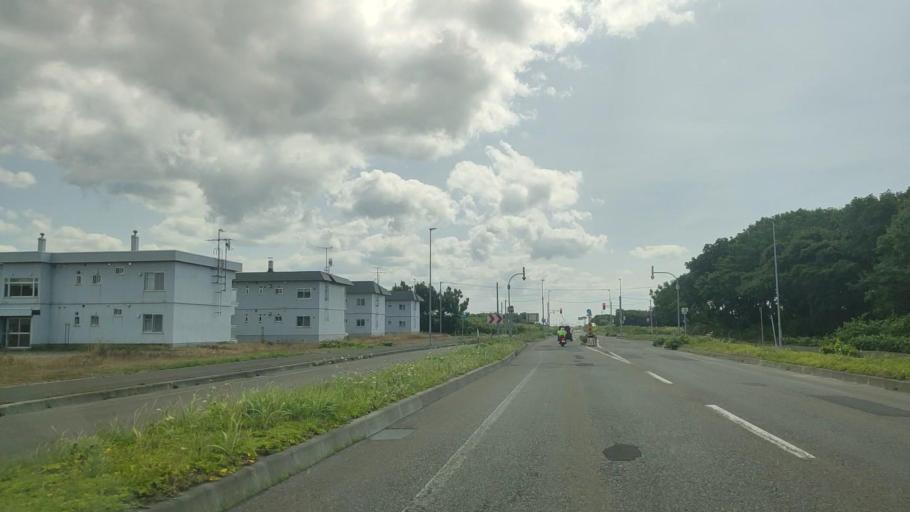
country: JP
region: Hokkaido
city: Makubetsu
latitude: 44.8787
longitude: 141.7502
